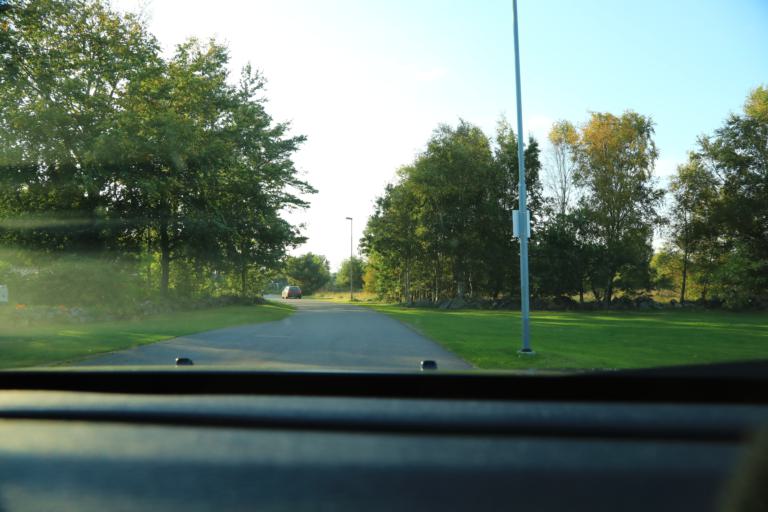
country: SE
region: Halland
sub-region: Varbergs Kommun
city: Traslovslage
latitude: 57.0482
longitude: 12.2936
